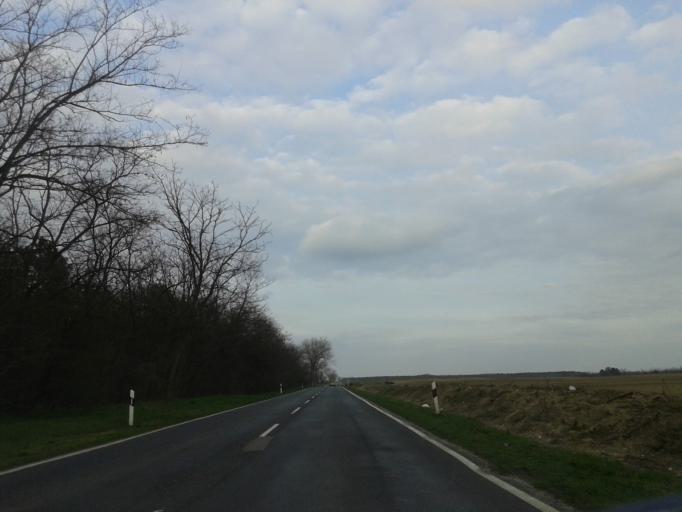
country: HU
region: Gyor-Moson-Sopron
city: Gyor
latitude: 47.7261
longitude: 17.7217
